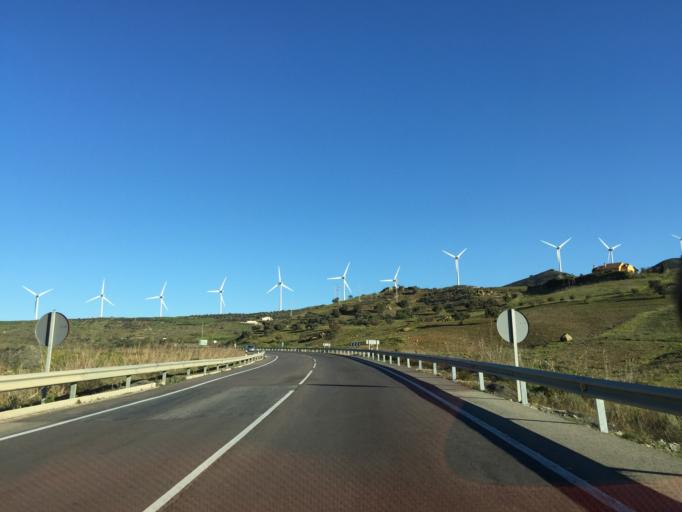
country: ES
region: Andalusia
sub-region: Provincia de Malaga
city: Carratraca
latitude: 36.8540
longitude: -4.8274
